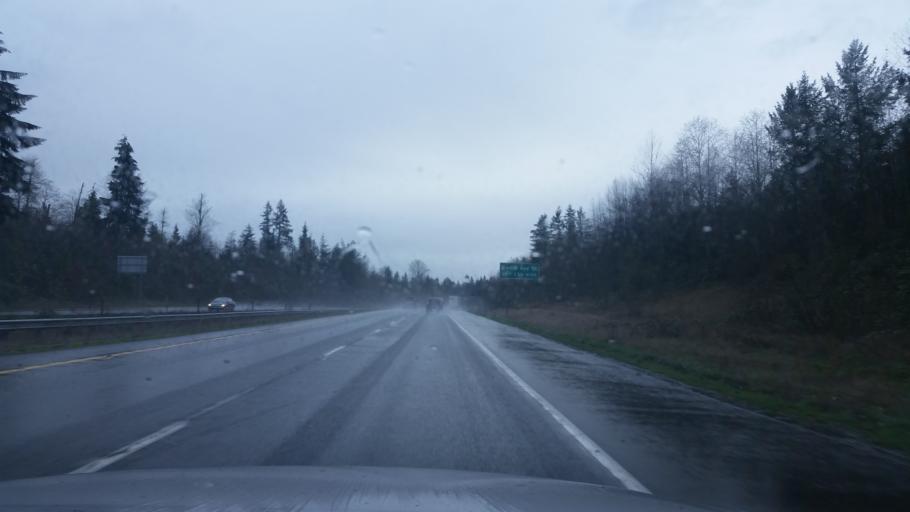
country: US
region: Washington
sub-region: King County
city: Hobart
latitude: 47.4276
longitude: -121.9902
